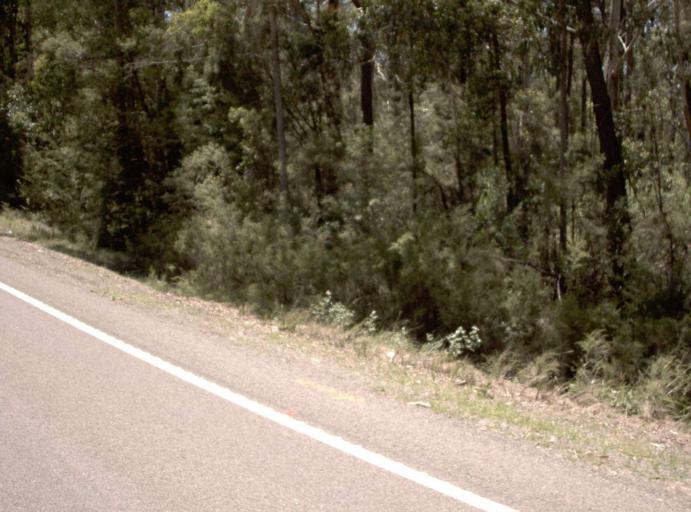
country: AU
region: Victoria
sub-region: East Gippsland
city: Lakes Entrance
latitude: -37.7658
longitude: 148.0585
